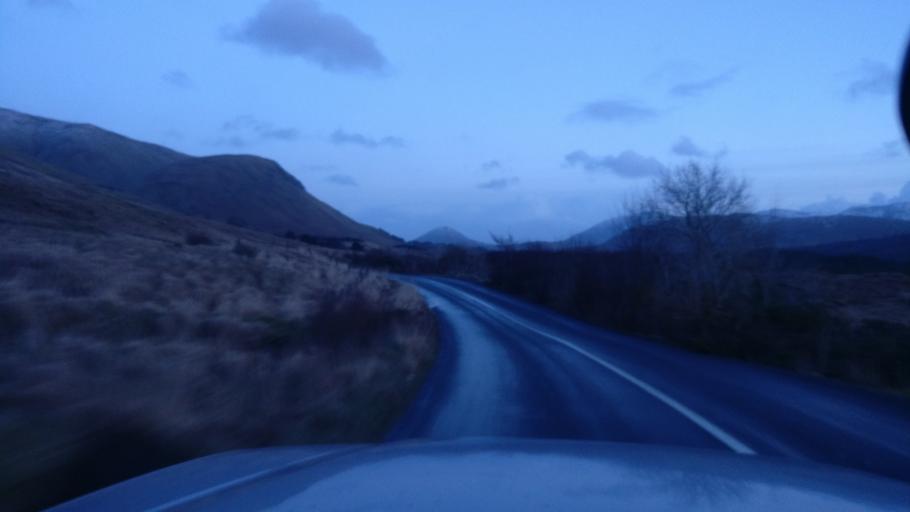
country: IE
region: Connaught
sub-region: Maigh Eo
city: Westport
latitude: 53.5570
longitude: -9.6442
